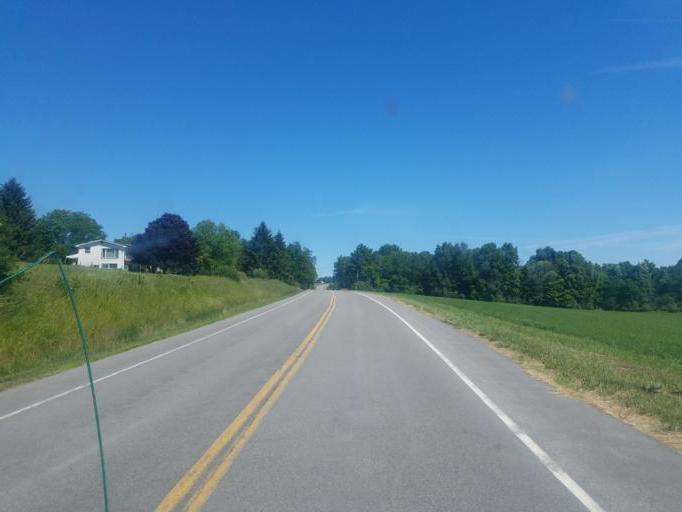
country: US
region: New York
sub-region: Ontario County
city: Canandaigua
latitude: 42.7176
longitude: -77.2760
